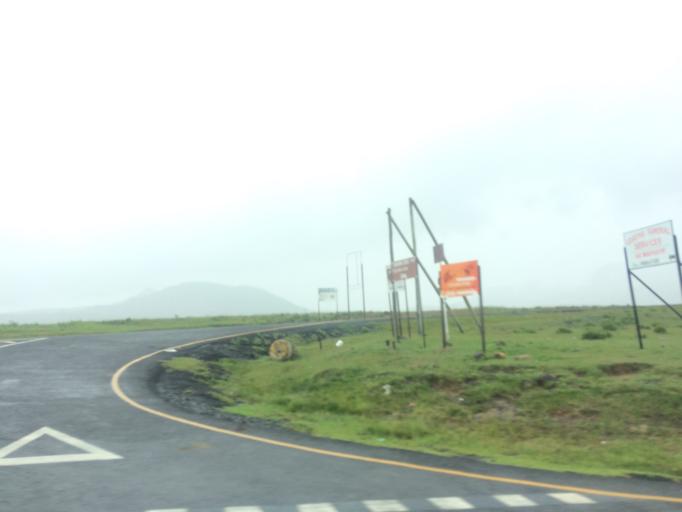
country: LS
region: Maseru
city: Nako
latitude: -29.7432
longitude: 27.5173
